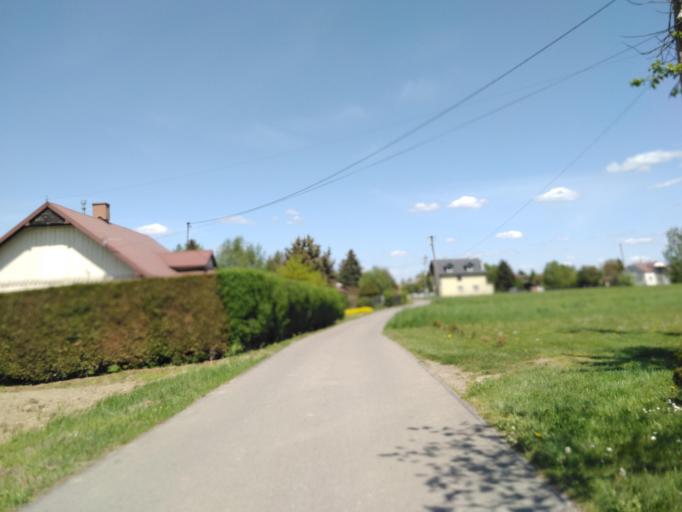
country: PL
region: Subcarpathian Voivodeship
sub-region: Powiat krosnienski
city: Chorkowka
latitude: 49.6805
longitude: 21.6963
